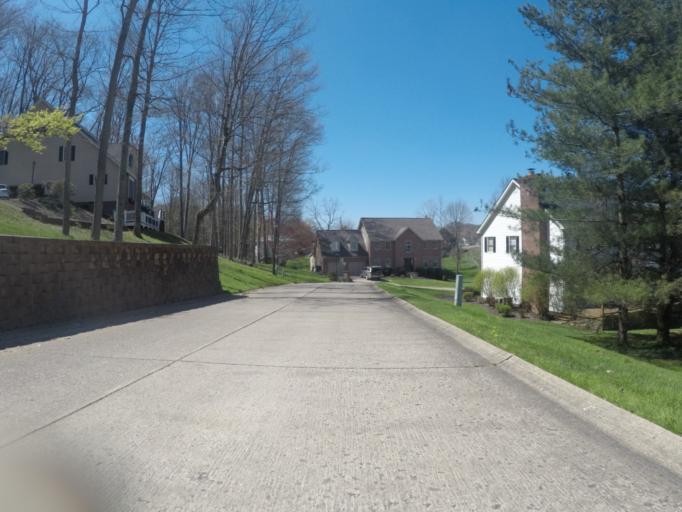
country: US
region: West Virginia
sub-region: Cabell County
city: Pea Ridge
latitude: 38.4213
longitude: -82.3171
